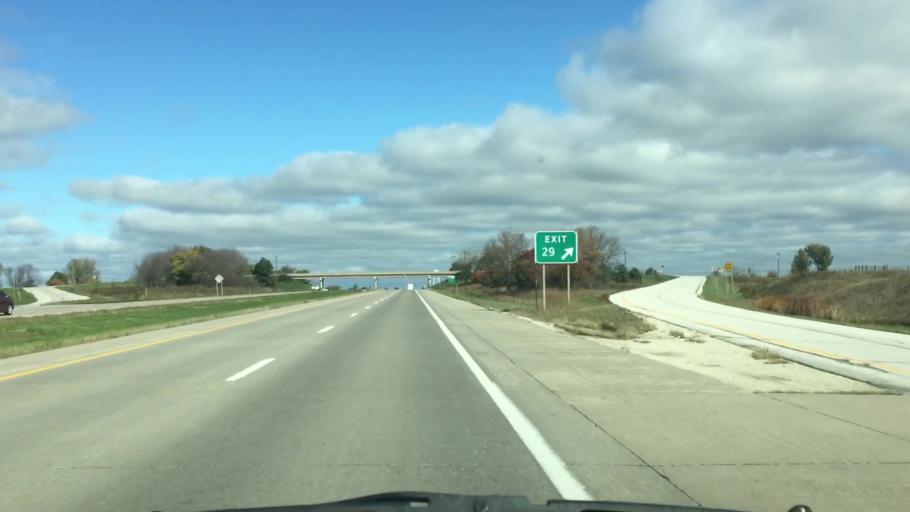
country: US
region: Iowa
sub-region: Clarke County
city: Osceola
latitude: 40.9688
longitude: -93.7972
